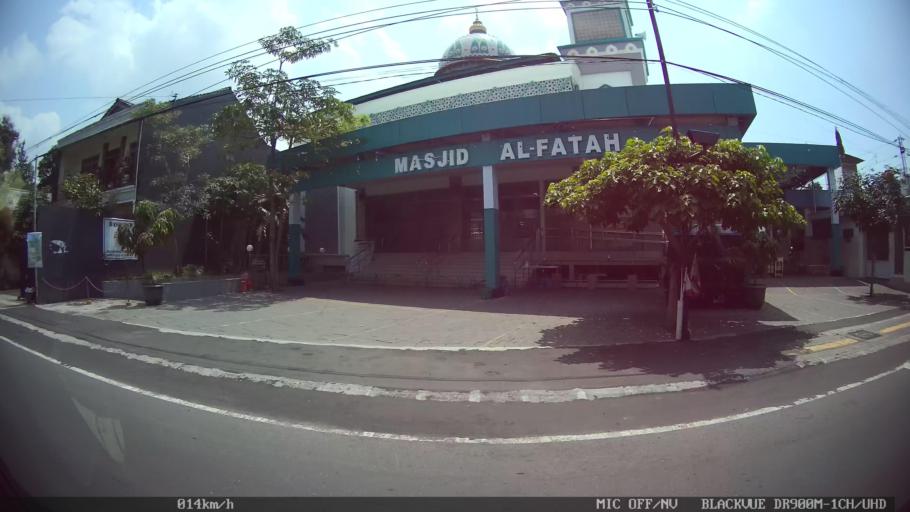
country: ID
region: Daerah Istimewa Yogyakarta
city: Yogyakarta
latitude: -7.8105
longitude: 110.3978
